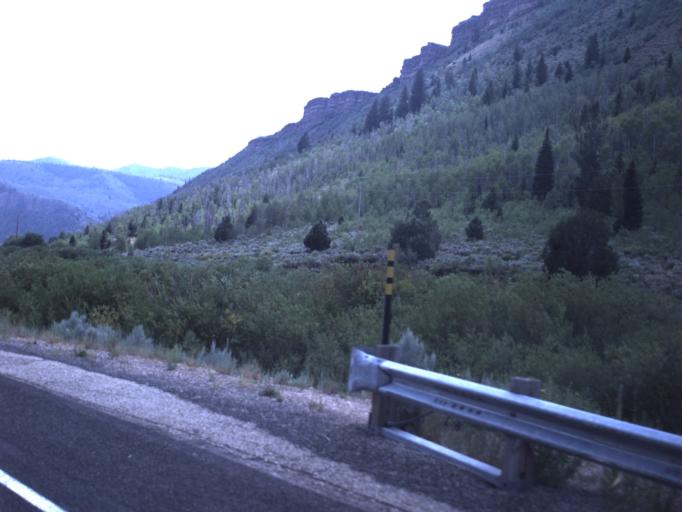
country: US
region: Utah
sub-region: Summit County
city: Francis
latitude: 40.4648
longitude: -110.8985
